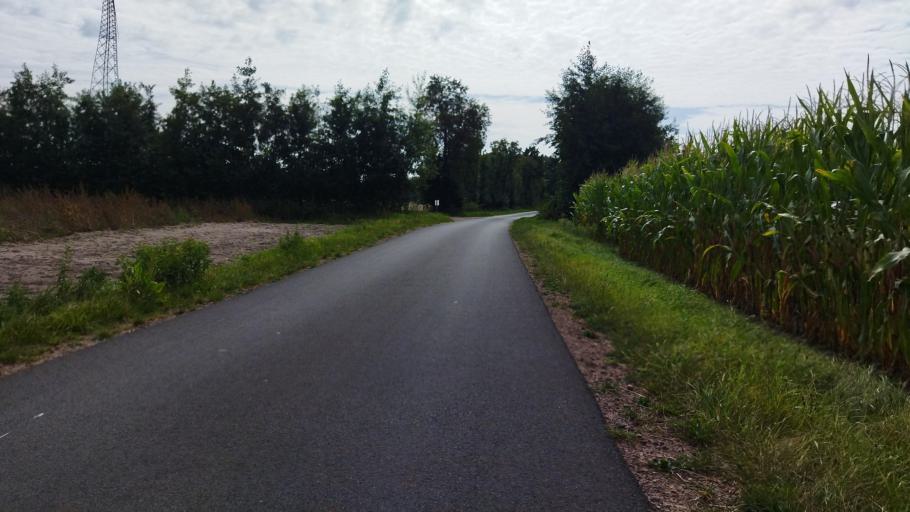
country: DE
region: Lower Saxony
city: Glandorf
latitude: 52.1158
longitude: 8.0003
